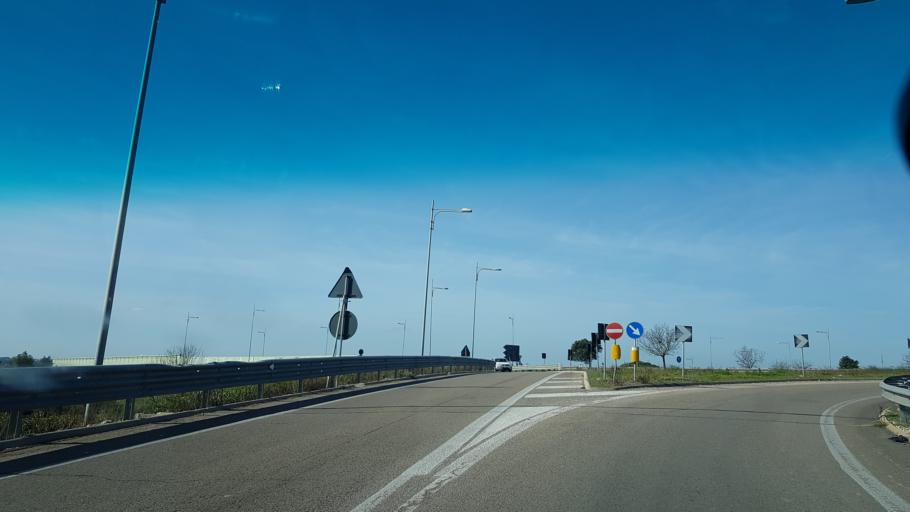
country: IT
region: Apulia
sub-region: Provincia di Lecce
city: Giorgilorio
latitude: 40.3562
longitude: 18.1375
